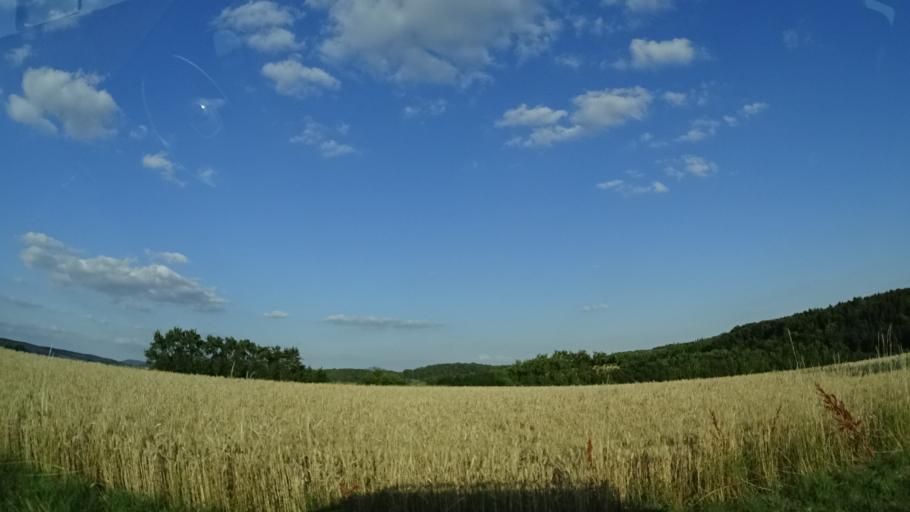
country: DE
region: Thuringia
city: Henneberg
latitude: 50.4500
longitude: 10.3631
